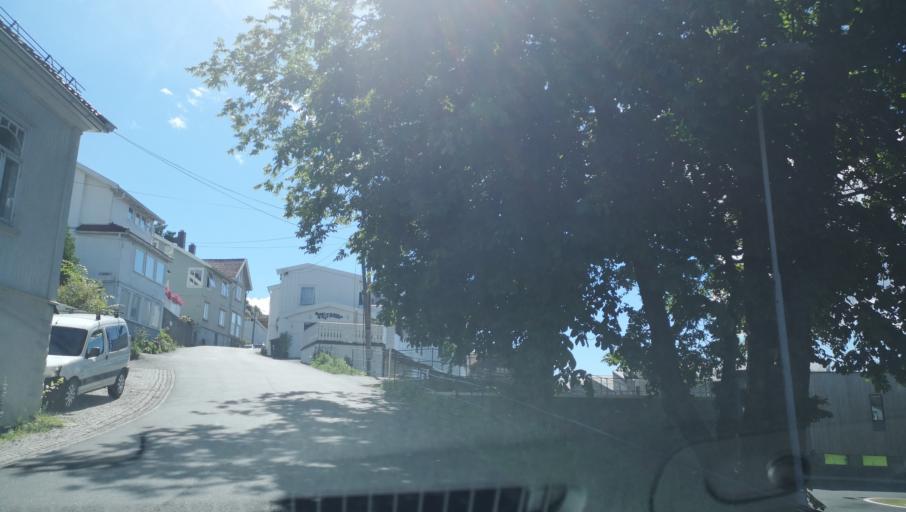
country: NO
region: Akershus
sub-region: Frogn
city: Drobak
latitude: 59.6583
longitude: 10.6306
